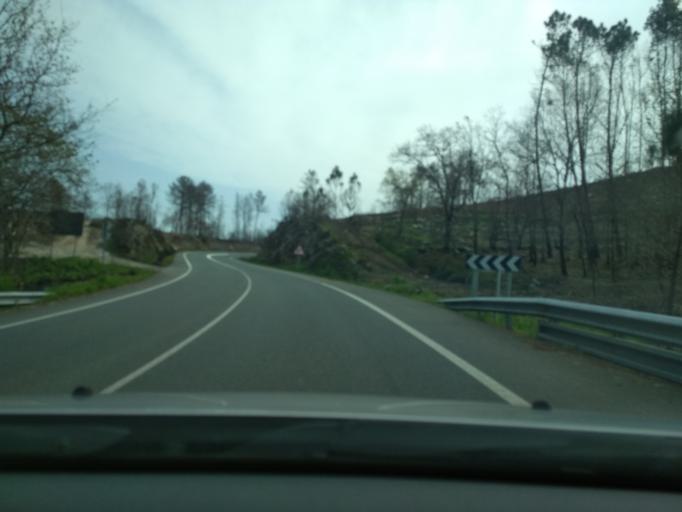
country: ES
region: Galicia
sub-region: Provincia de Pontevedra
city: Catoira
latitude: 42.6521
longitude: -8.6857
